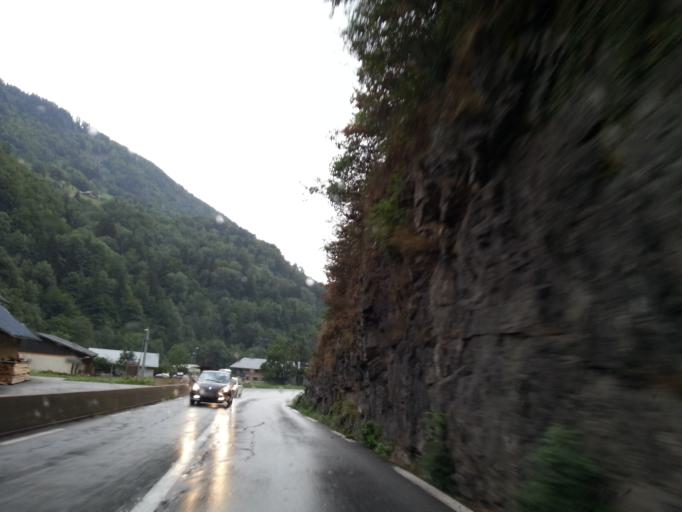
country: FR
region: Rhone-Alpes
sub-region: Departement de la Savoie
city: Marthod
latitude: 45.7178
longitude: 6.4473
